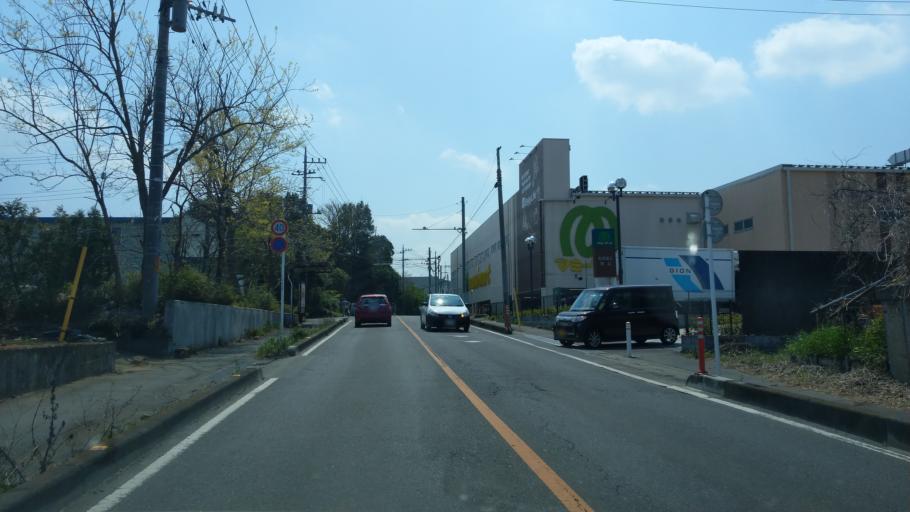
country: JP
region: Saitama
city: Saitama
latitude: 35.8938
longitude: 139.6652
